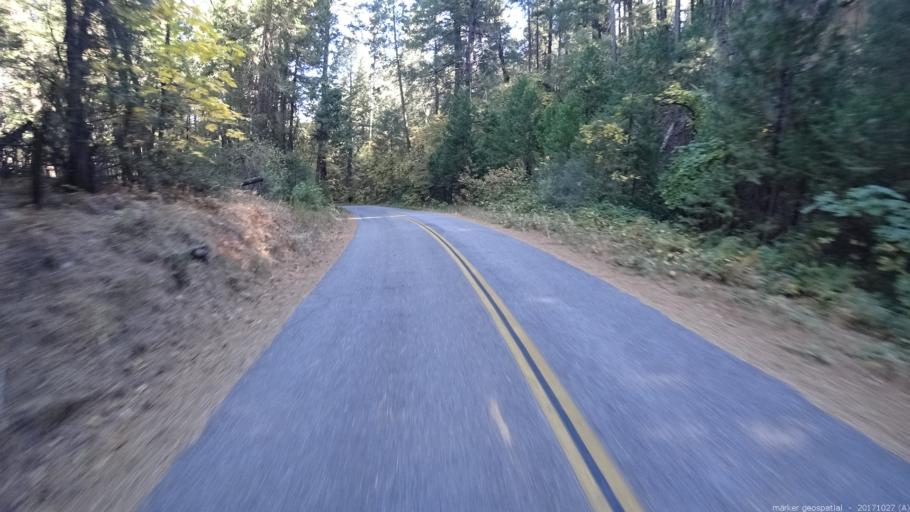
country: US
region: California
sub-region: Shasta County
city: Shingletown
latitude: 40.7425
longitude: -121.9503
